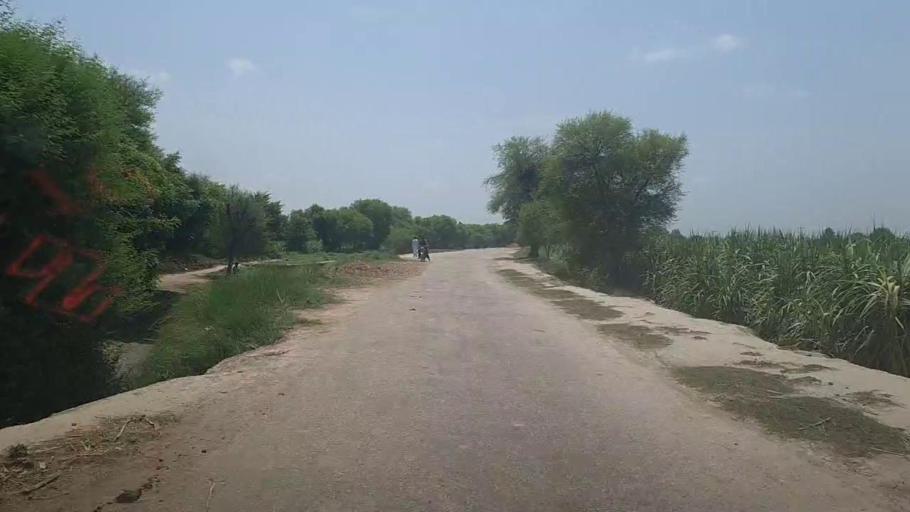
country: PK
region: Sindh
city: Ubauro
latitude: 28.2848
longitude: 69.8089
